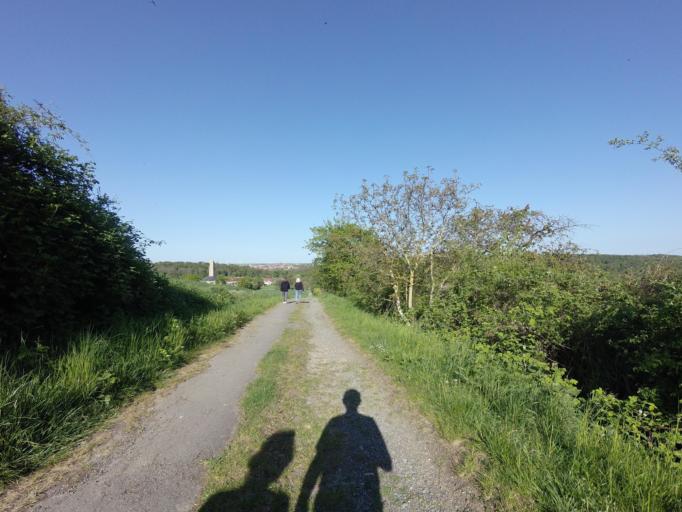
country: DE
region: Lower Saxony
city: Hildesheim
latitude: 52.1364
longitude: 9.9171
